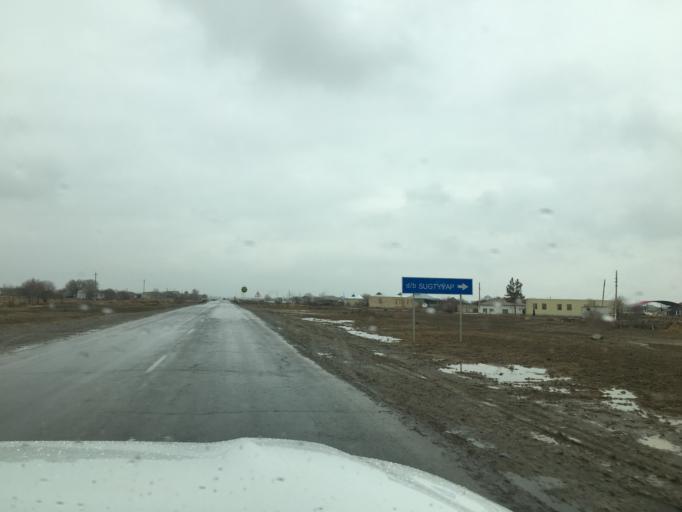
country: TM
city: Murgab
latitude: 37.4687
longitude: 62.0330
